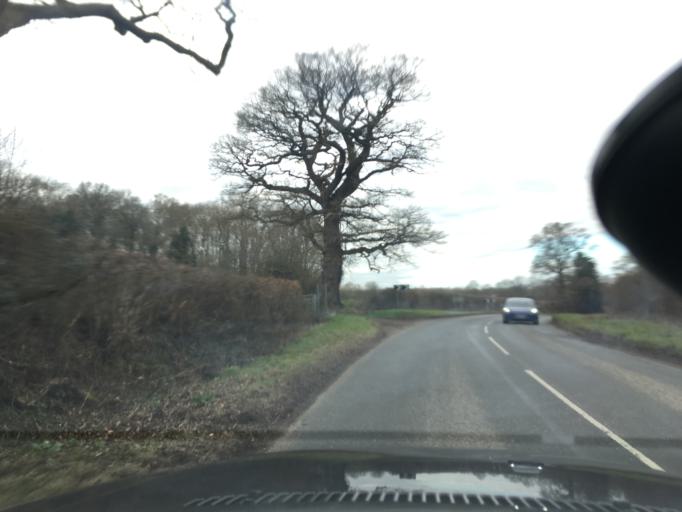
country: GB
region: England
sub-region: West Berkshire
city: Stratfield Mortimer
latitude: 51.3220
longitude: -1.0360
